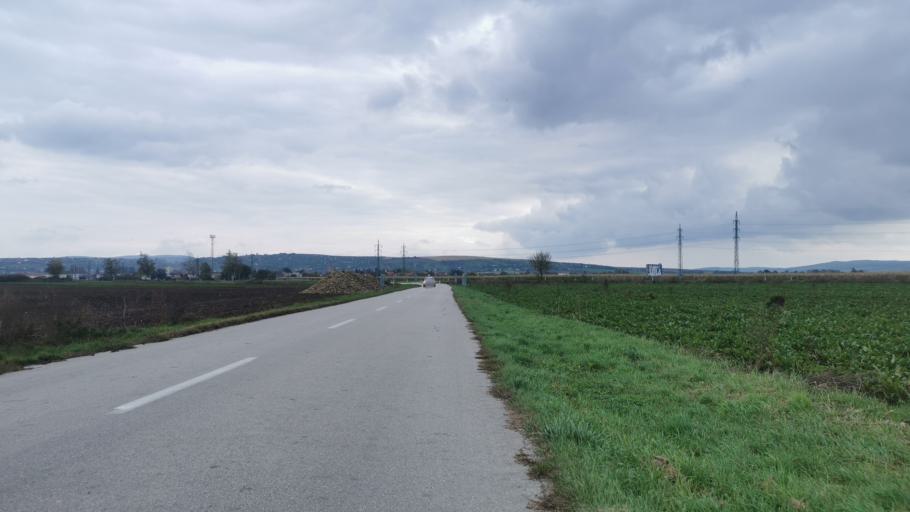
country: SK
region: Trnavsky
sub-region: Okres Skalica
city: Holic
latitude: 48.8278
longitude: 17.1783
